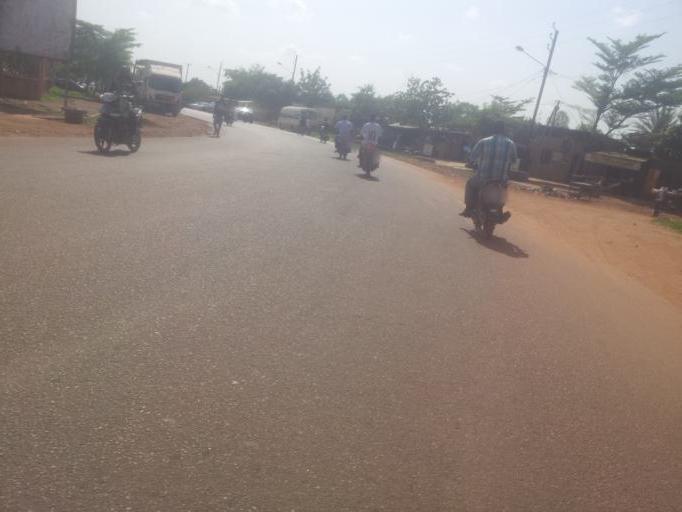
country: BF
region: Centre
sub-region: Kadiogo Province
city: Ouagadougou
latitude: 12.3630
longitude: -1.5575
